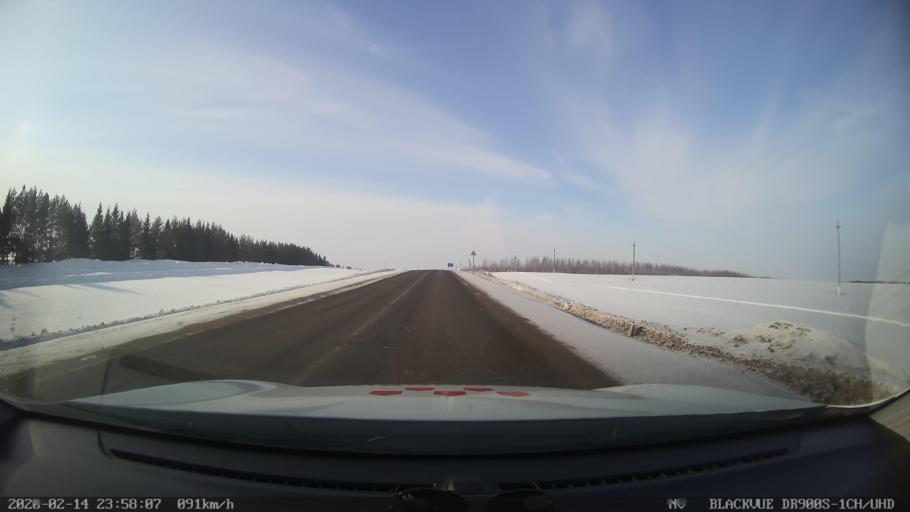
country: RU
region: Tatarstan
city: Kuybyshevskiy Zaton
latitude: 55.3387
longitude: 49.0948
